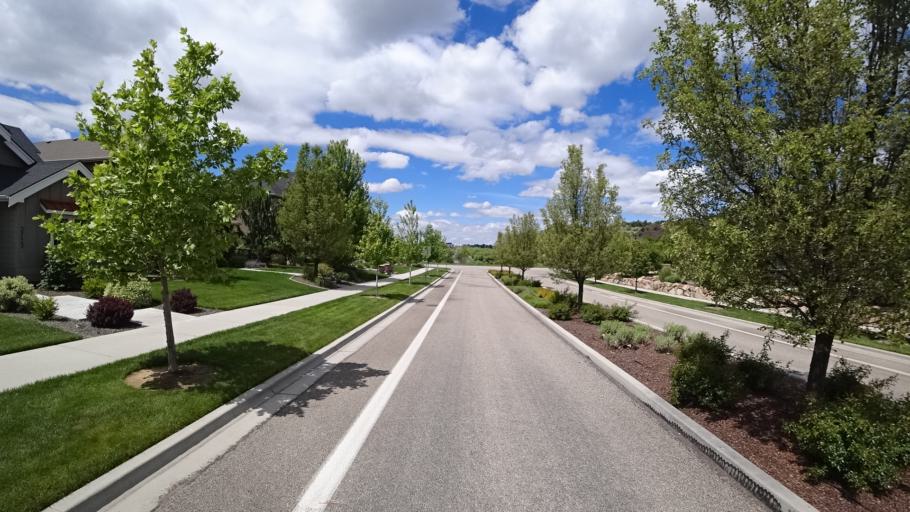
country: US
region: Idaho
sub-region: Ada County
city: Boise
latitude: 43.5779
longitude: -116.1380
